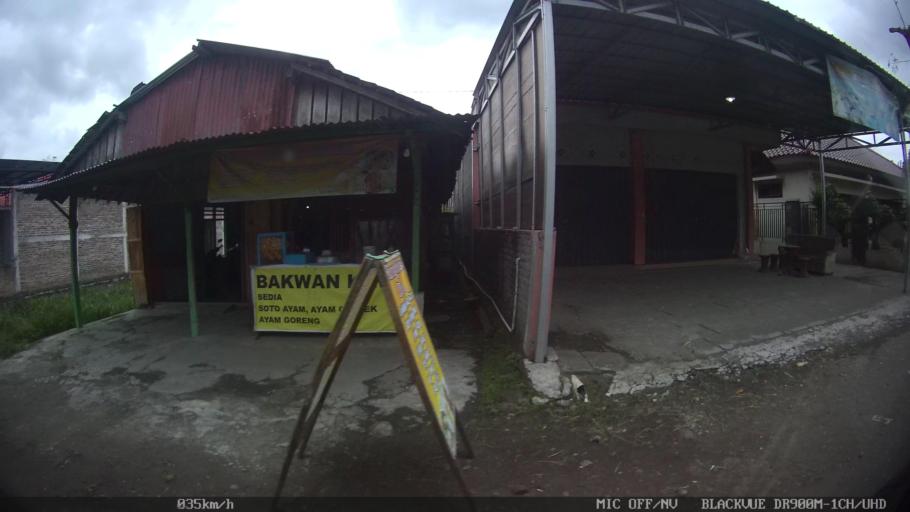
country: ID
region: Daerah Istimewa Yogyakarta
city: Sewon
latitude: -7.8750
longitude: 110.4071
